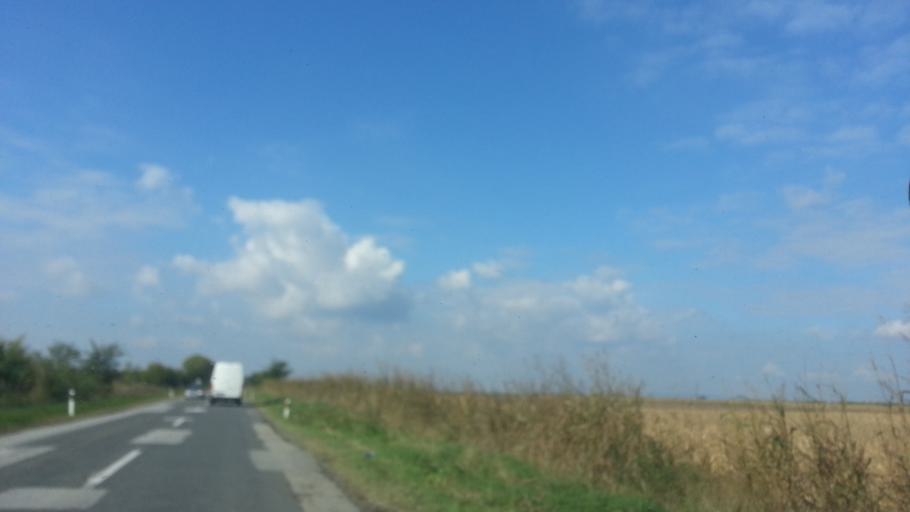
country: RS
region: Autonomna Pokrajina Vojvodina
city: Nova Pazova
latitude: 44.9865
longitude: 20.2298
